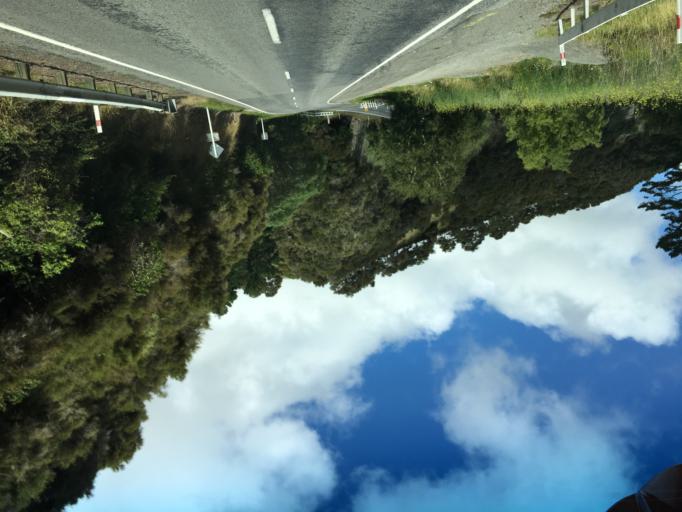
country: NZ
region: Hawke's Bay
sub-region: Napier City
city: Napier
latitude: -39.1289
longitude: 176.9967
